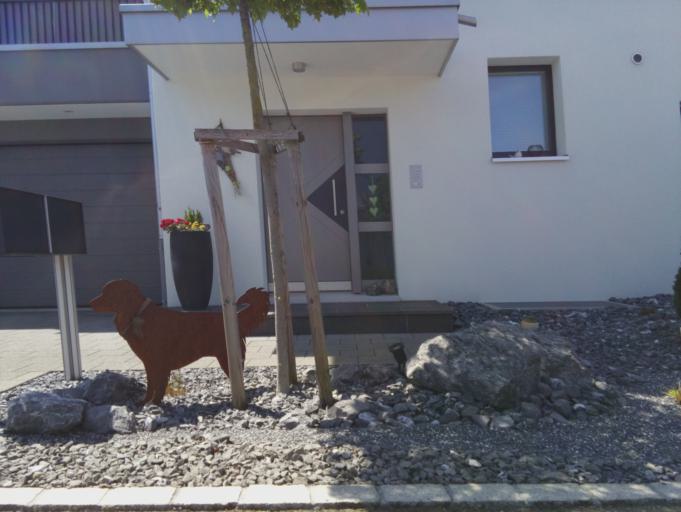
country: CH
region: Schwyz
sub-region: Bezirk March
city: Schubelbach
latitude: 47.1887
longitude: 8.9019
